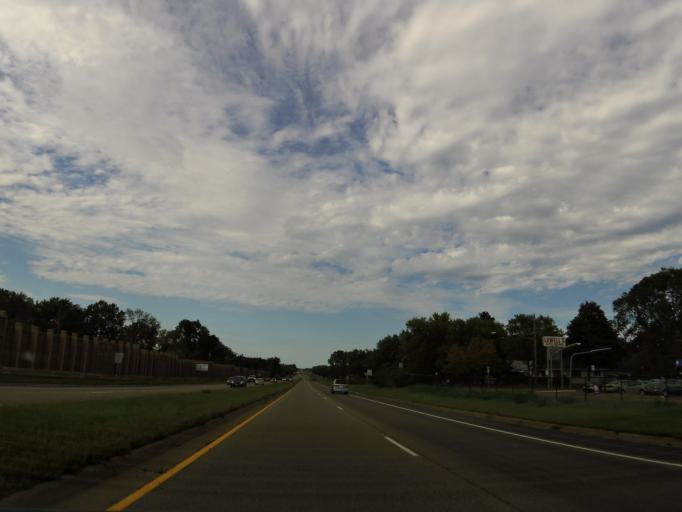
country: US
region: Minnesota
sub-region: Anoka County
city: Columbia Heights
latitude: 45.0492
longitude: -93.2631
